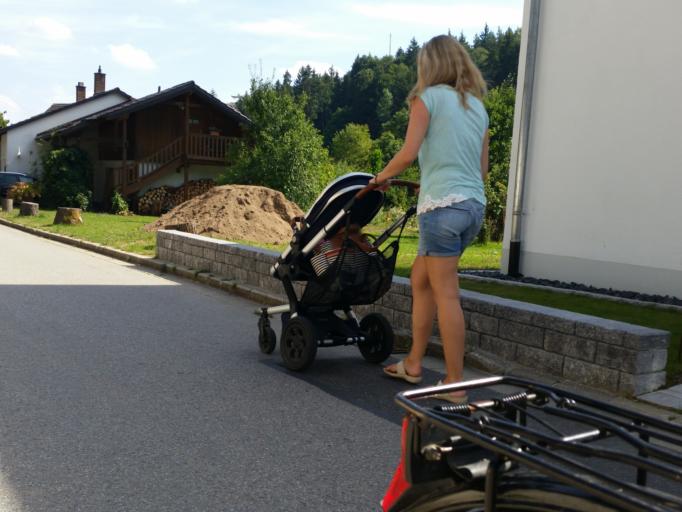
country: DE
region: Bavaria
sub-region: Upper Palatinate
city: Kastl
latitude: 49.3713
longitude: 11.6734
